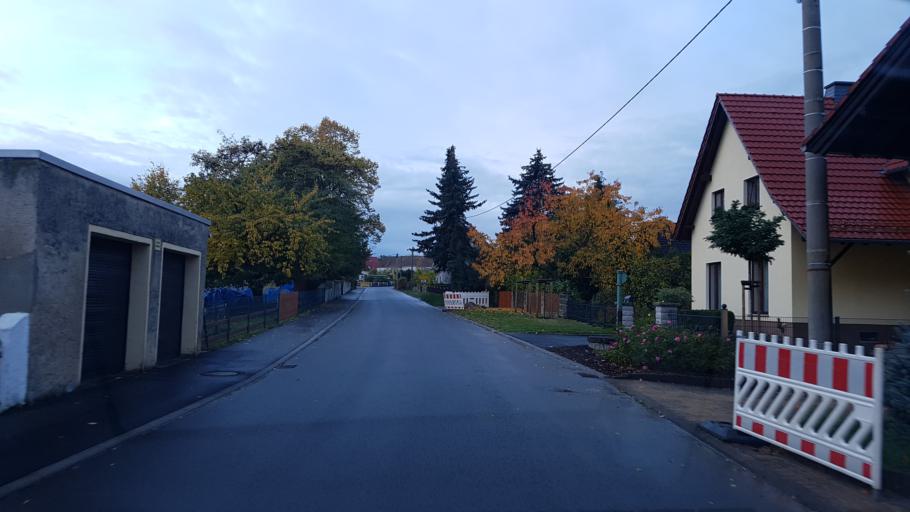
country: DE
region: Saxony
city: Dahlen
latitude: 51.3900
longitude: 13.0592
